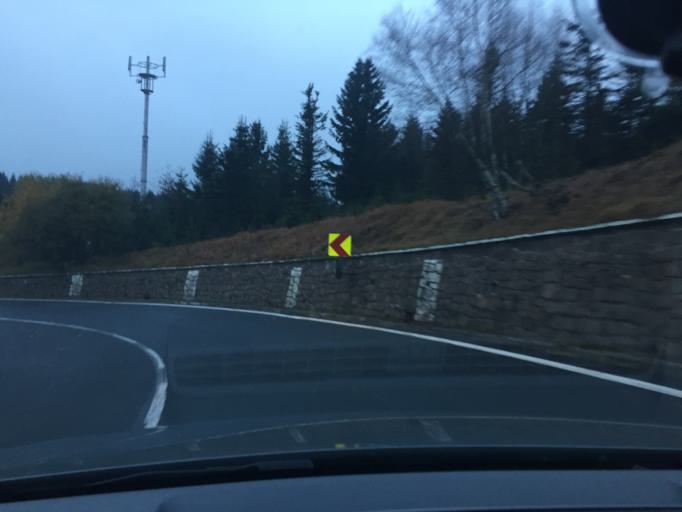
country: DE
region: Saxony
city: Altenberg
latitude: 50.7245
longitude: 13.7575
